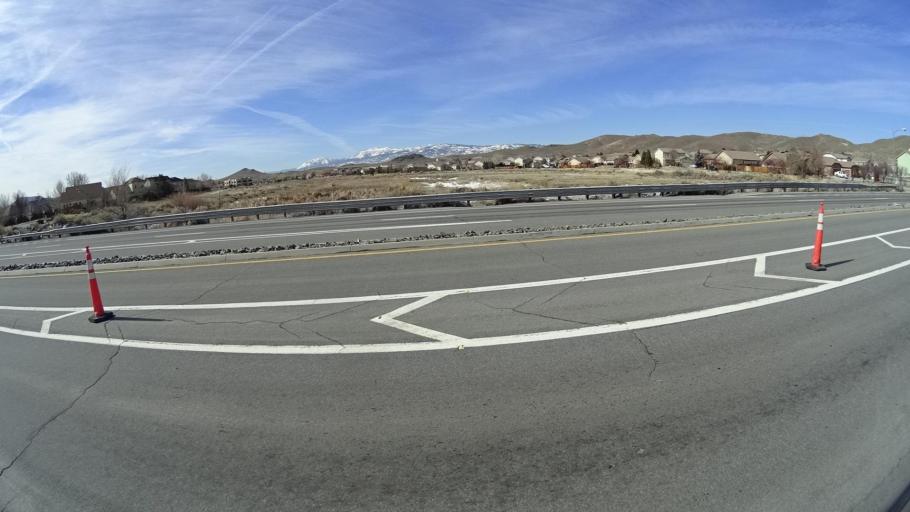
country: US
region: Nevada
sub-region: Washoe County
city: Sun Valley
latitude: 39.5901
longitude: -119.7287
